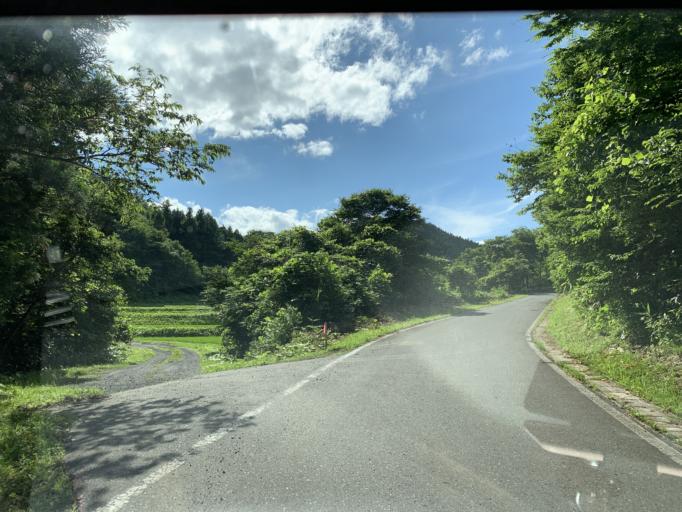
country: JP
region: Iwate
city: Ichinoseki
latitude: 38.9212
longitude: 140.9606
